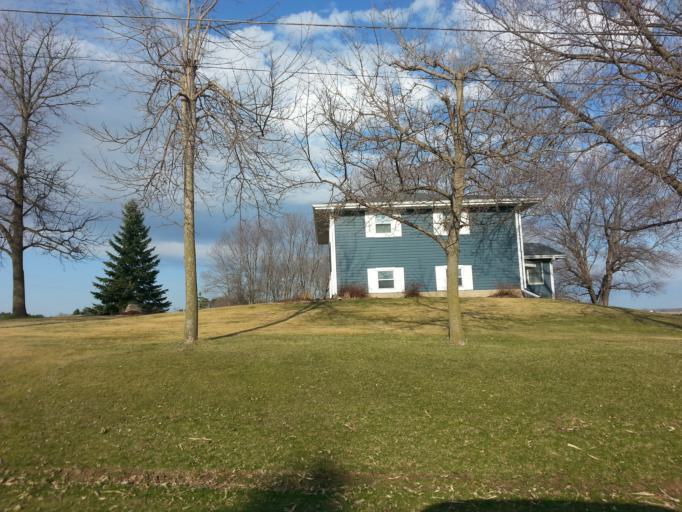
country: US
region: Minnesota
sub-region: Washington County
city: Afton
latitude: 44.8335
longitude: -92.8419
